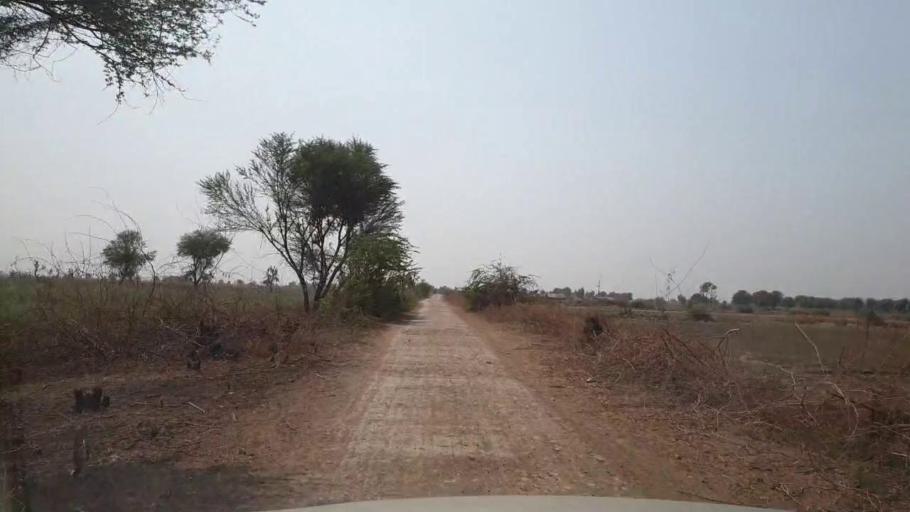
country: PK
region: Sindh
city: Dhoro Naro
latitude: 25.4591
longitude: 69.6275
